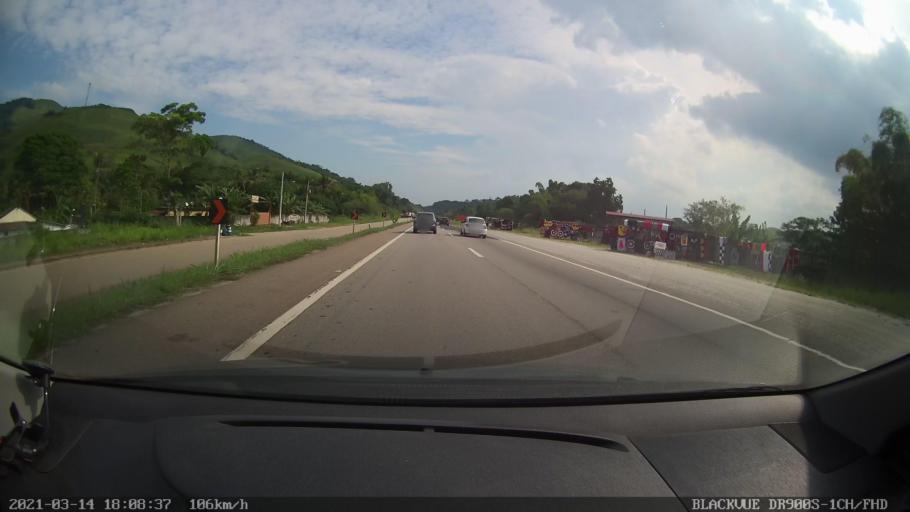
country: BR
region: Rio de Janeiro
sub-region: Petropolis
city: Petropolis
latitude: -22.5801
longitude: -43.2744
